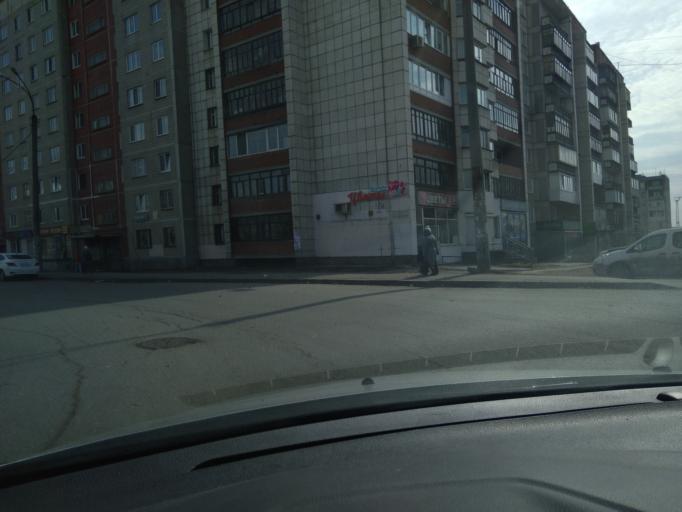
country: RU
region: Sverdlovsk
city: Shuvakish
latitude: 56.8713
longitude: 60.5199
